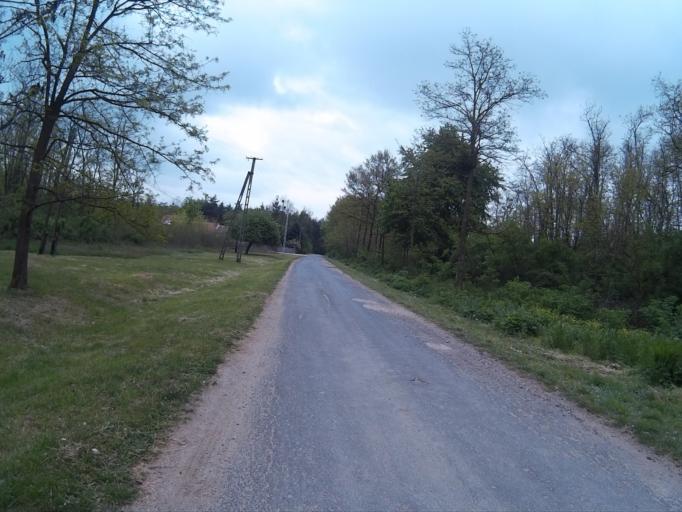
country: HU
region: Vas
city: Vasvar
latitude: 47.0556
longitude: 16.8549
